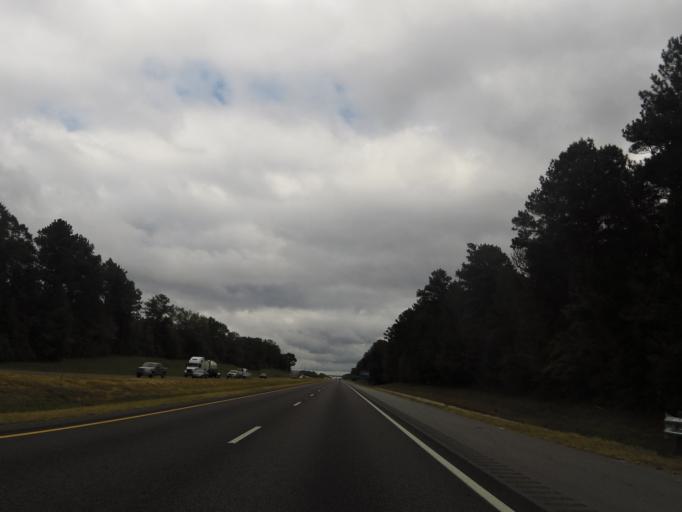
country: US
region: Alabama
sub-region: Conecuh County
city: Evergreen
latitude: 31.4492
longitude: -86.9724
